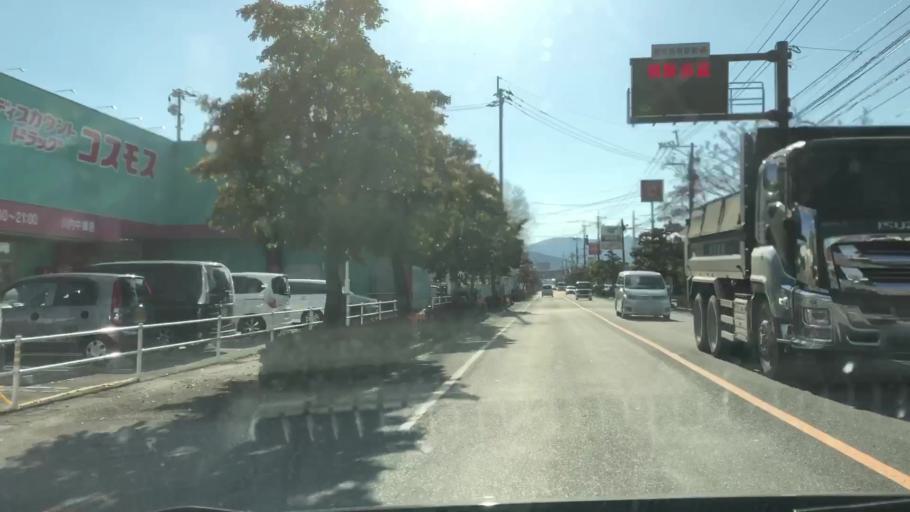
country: JP
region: Kagoshima
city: Satsumasendai
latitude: 31.8348
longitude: 130.3115
